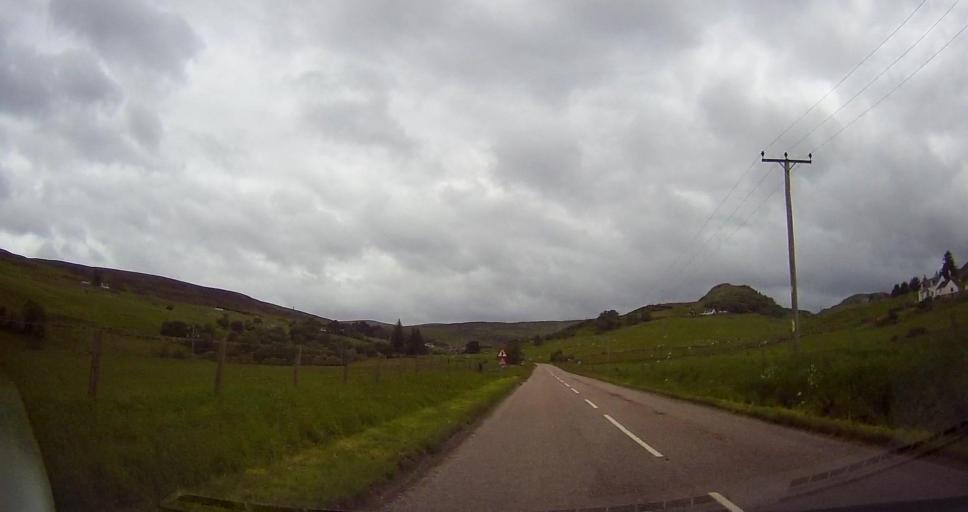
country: GB
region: Scotland
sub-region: Highland
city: Dornoch
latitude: 58.0071
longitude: -4.2441
